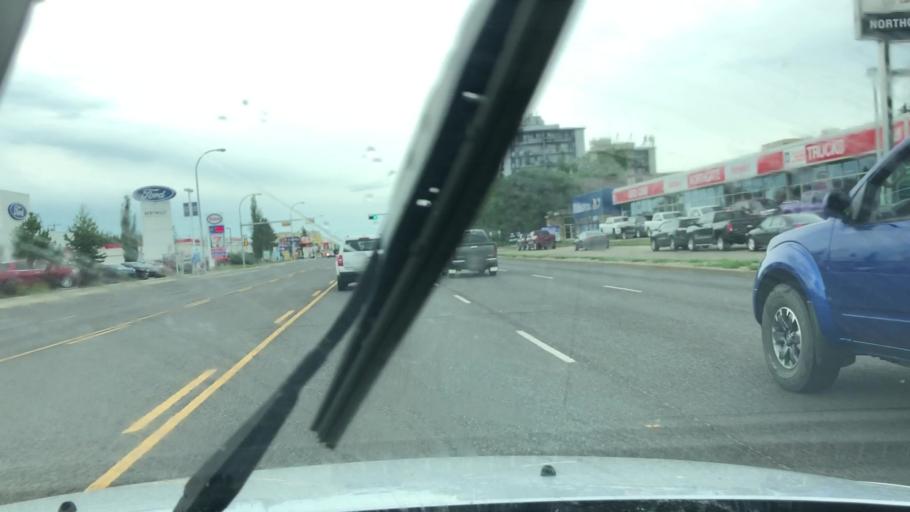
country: CA
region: Alberta
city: Edmonton
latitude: 53.5936
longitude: -113.4920
